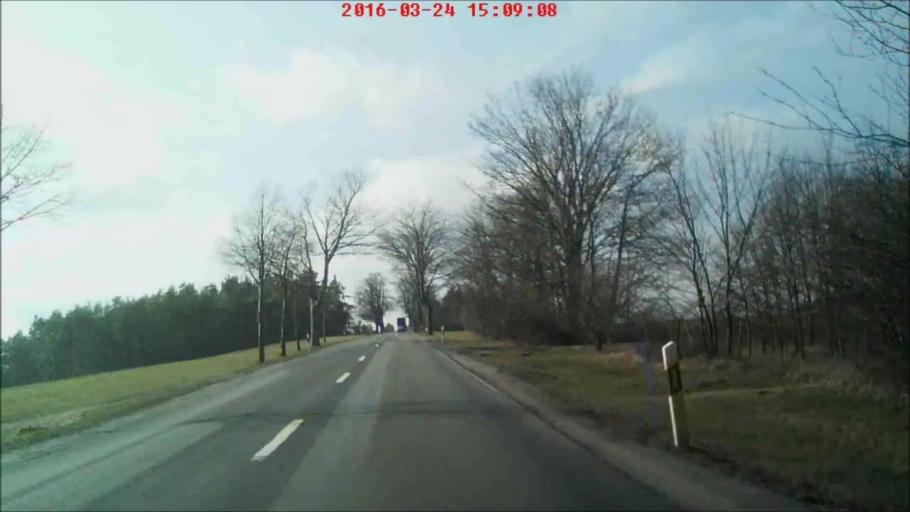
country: DE
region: Thuringia
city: Stadtilm
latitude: 50.7622
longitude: 11.1251
